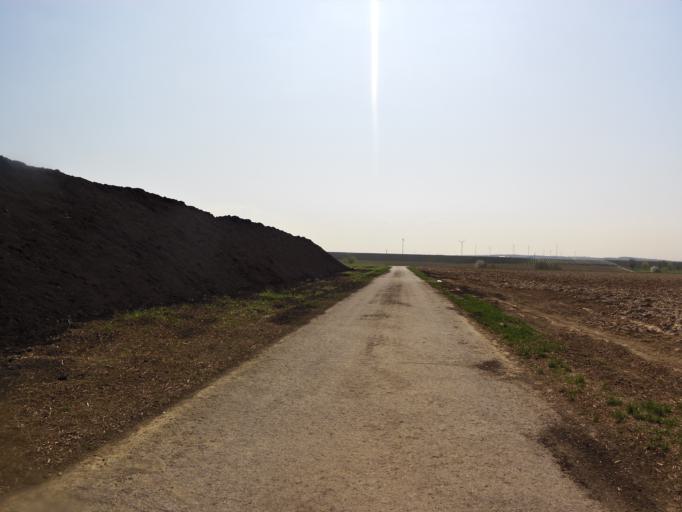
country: DE
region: Bavaria
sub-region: Regierungsbezirk Unterfranken
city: Mainstockheim
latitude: 49.8152
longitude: 10.1149
